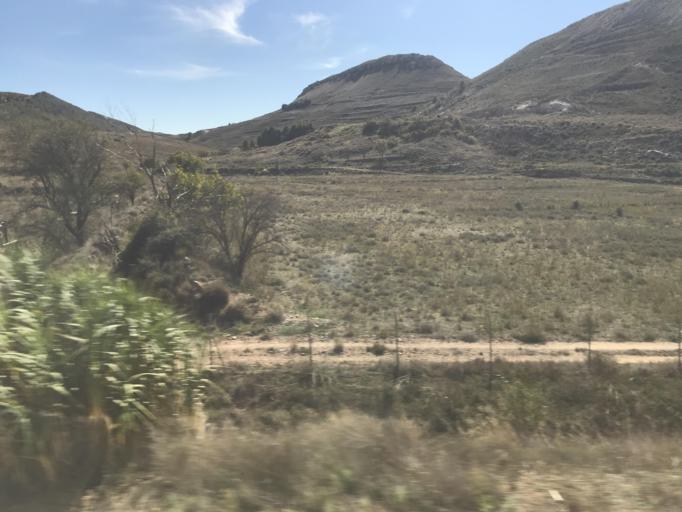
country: ES
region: Aragon
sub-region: Provincia de Zaragoza
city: Alhama de Aragon
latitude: 41.2971
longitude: -1.8711
